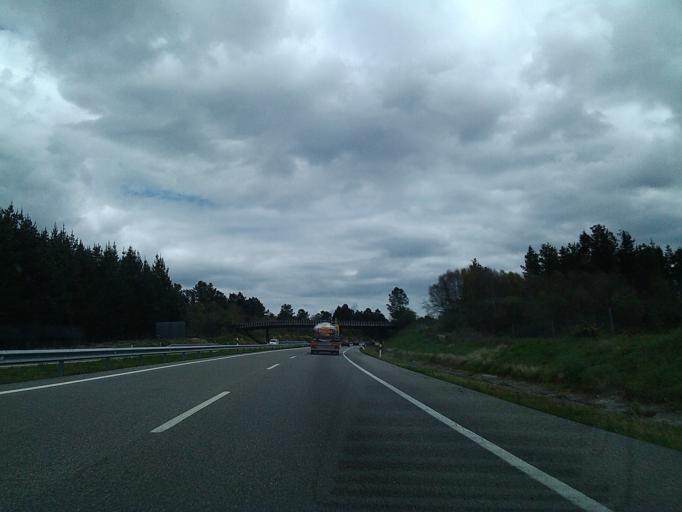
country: ES
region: Galicia
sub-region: Provincia de Lugo
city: Guitiriz
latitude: 43.1927
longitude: -7.8775
